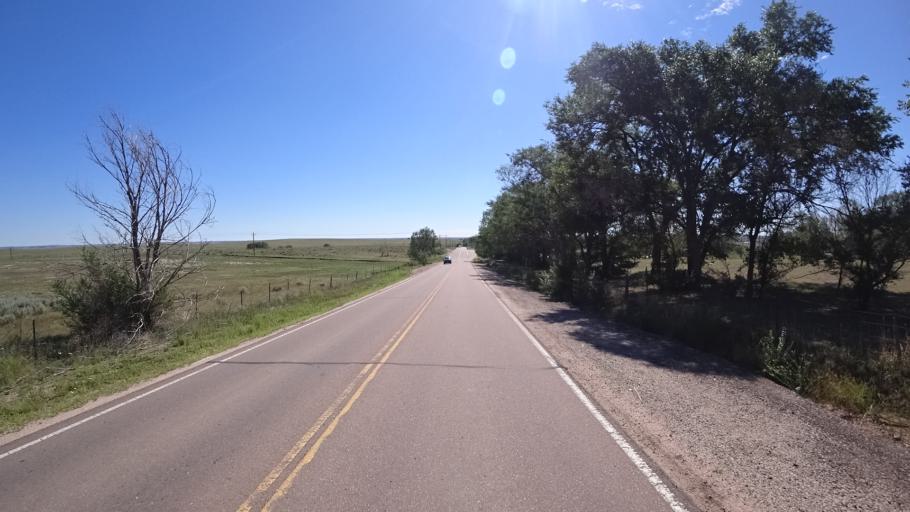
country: US
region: Colorado
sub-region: El Paso County
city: Security-Widefield
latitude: 38.7374
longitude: -104.6753
